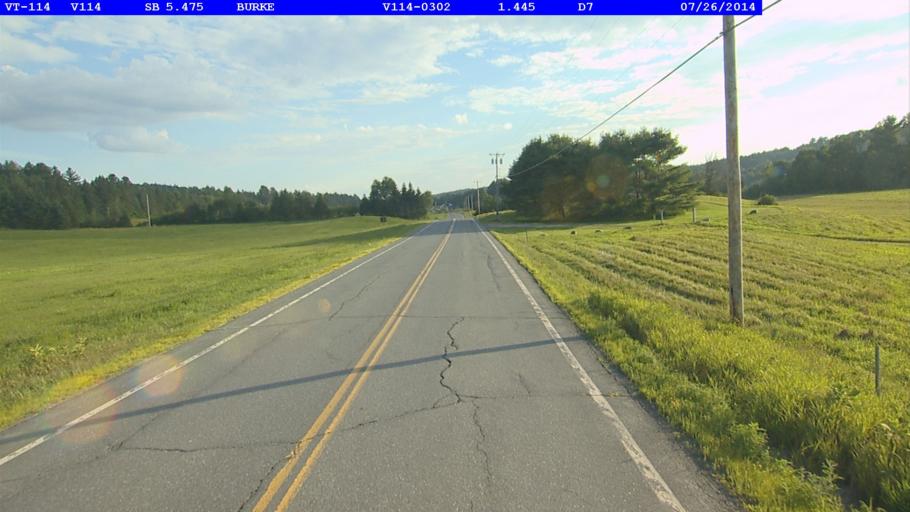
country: US
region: Vermont
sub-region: Caledonia County
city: Lyndonville
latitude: 44.5980
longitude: -71.9322
